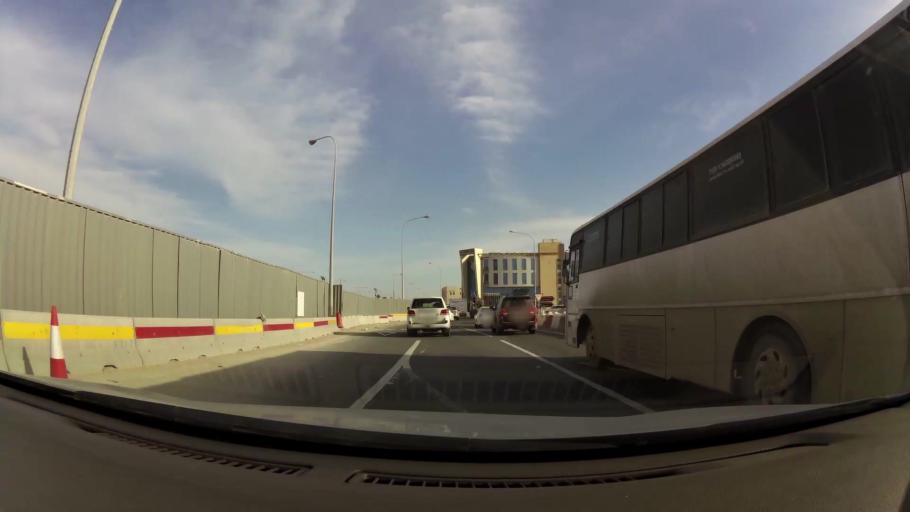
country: QA
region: Al Wakrah
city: Al Wakrah
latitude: 25.1923
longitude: 51.5961
